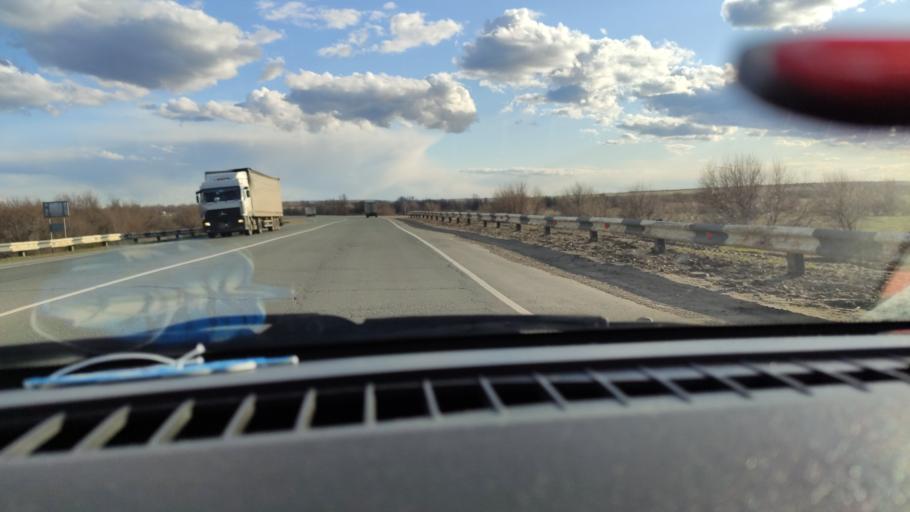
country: RU
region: Saratov
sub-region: Saratovskiy Rayon
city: Saratov
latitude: 51.7190
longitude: 46.0263
